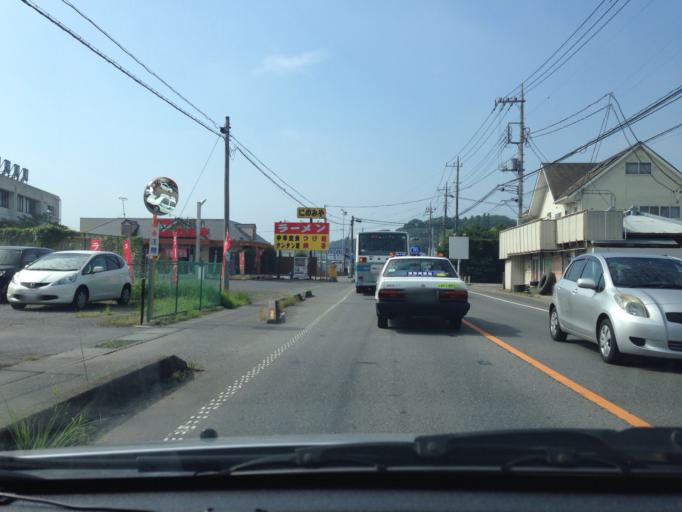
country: JP
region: Ibaraki
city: Ami
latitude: 36.0523
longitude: 140.2157
